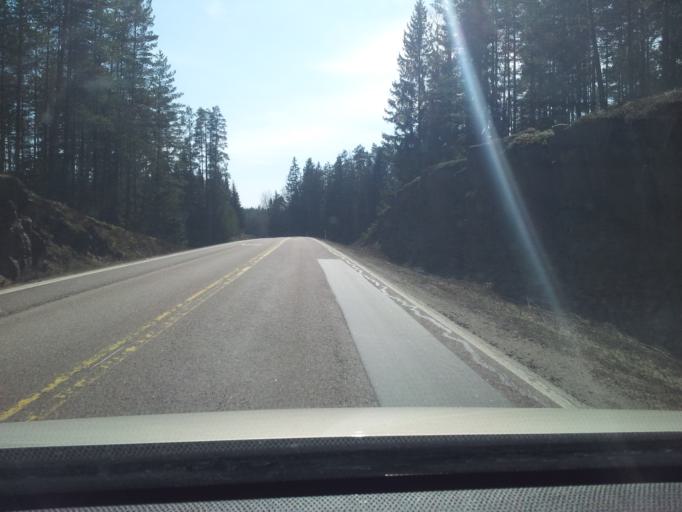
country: FI
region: Kymenlaakso
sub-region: Kotka-Hamina
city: Hamina
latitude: 60.7463
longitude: 27.3306
